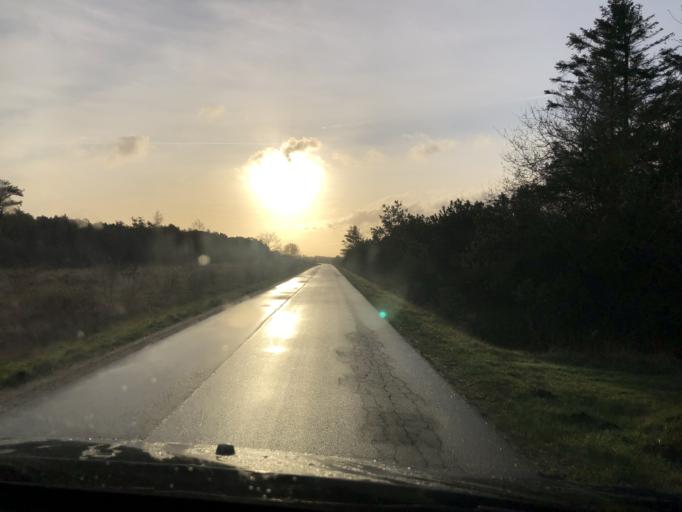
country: DK
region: Central Jutland
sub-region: Ringkobing-Skjern Kommune
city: Skjern
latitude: 55.8653
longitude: 8.3682
